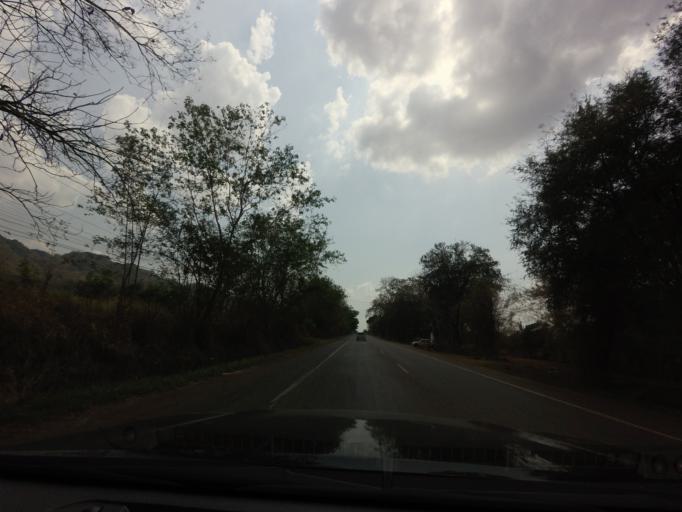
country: TH
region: Kanchanaburi
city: Sai Yok
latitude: 14.1577
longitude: 99.1388
